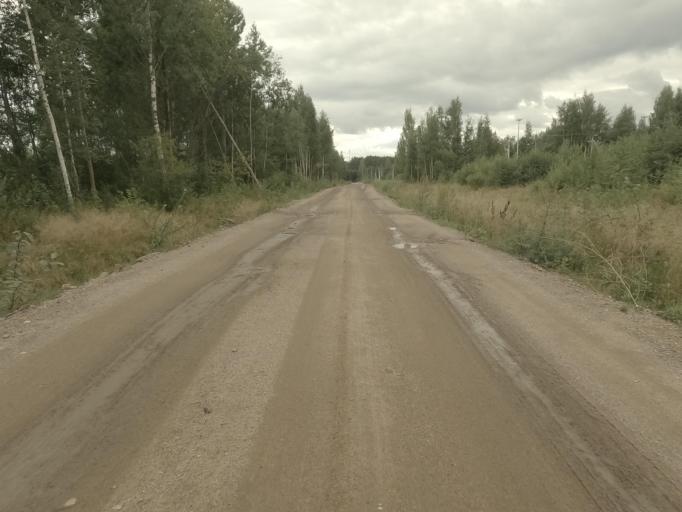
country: RU
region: Leningrad
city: Kirovsk
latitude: 59.9013
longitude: 31.0033
